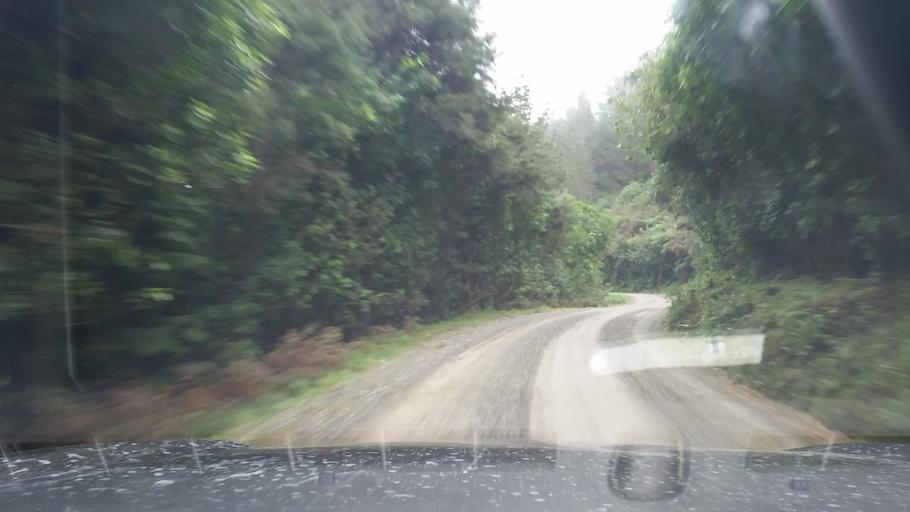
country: NZ
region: Marlborough
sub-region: Marlborough District
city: Picton
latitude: -41.1796
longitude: 173.9970
